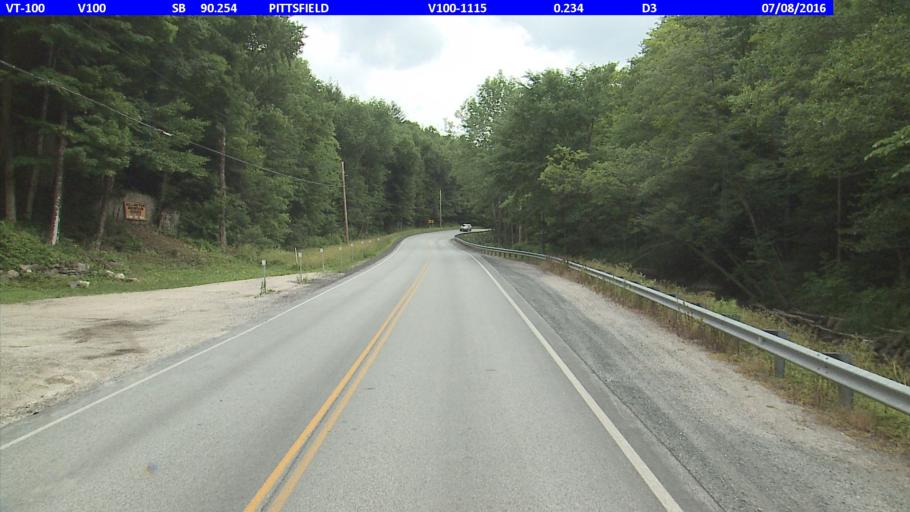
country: US
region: Vermont
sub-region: Rutland County
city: Rutland
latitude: 43.7209
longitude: -72.8228
